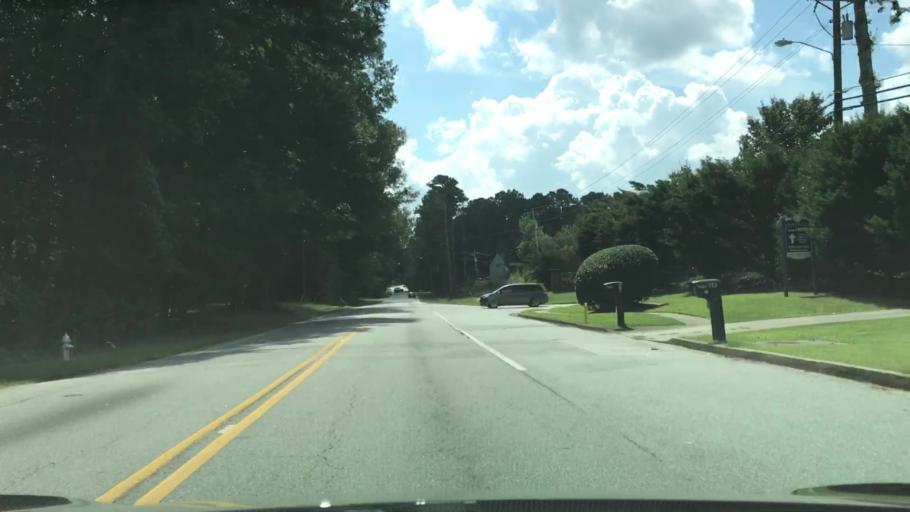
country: US
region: Georgia
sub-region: Gwinnett County
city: Lawrenceville
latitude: 33.9464
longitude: -84.0634
